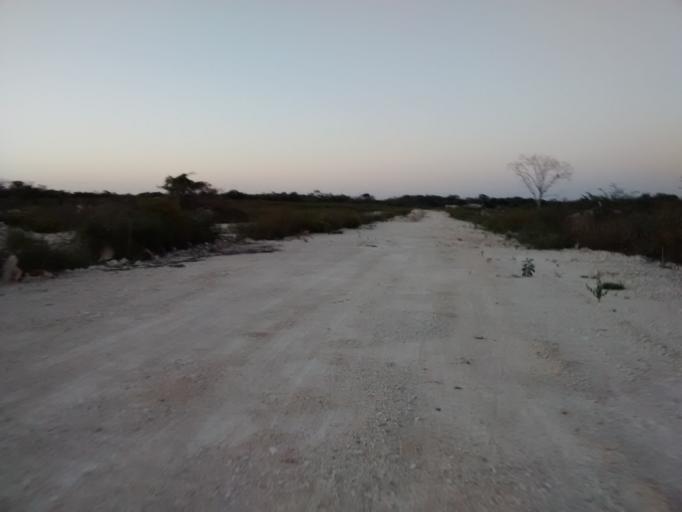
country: MX
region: Yucatan
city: Valladolid
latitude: 20.6794
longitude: -88.1723
